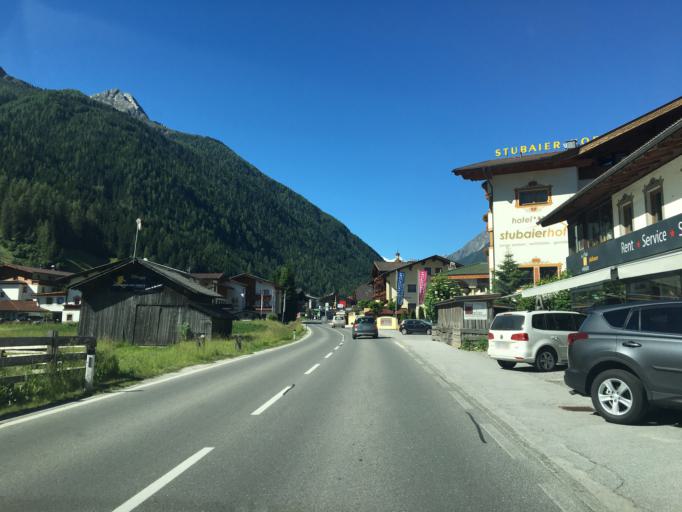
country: AT
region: Tyrol
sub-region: Politischer Bezirk Innsbruck Land
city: Neustift im Stubaital
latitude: 47.1137
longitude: 11.3114
